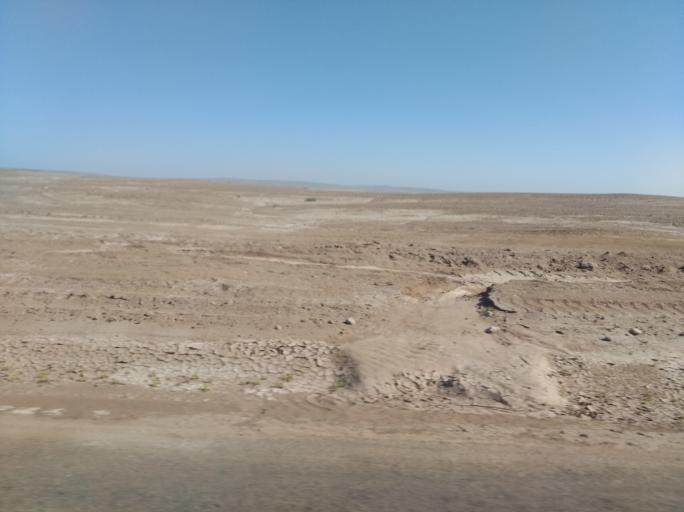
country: CL
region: Atacama
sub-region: Provincia de Copiapo
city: Copiapo
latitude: -27.3170
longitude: -70.8349
